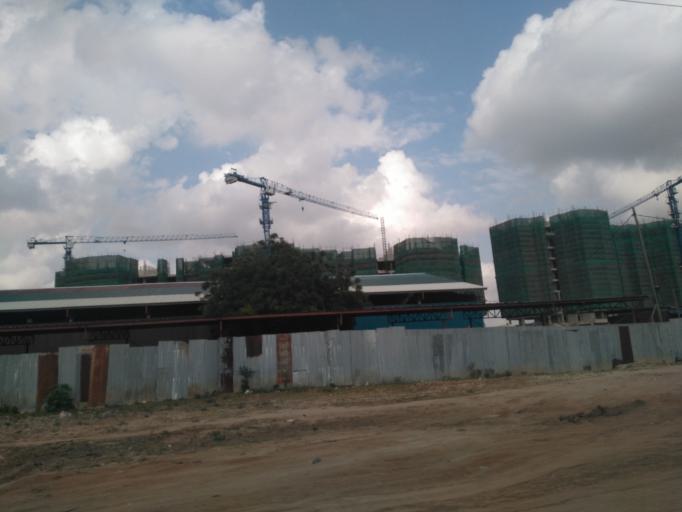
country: TZ
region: Dar es Salaam
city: Magomeni
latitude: -6.7392
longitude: 39.2388
